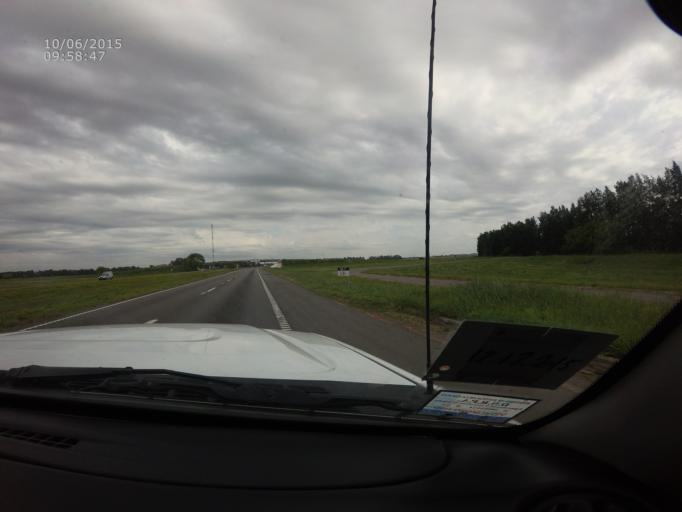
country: AR
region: Buenos Aires
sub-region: Partido de Baradero
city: Baradero
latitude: -33.9122
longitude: -59.4522
